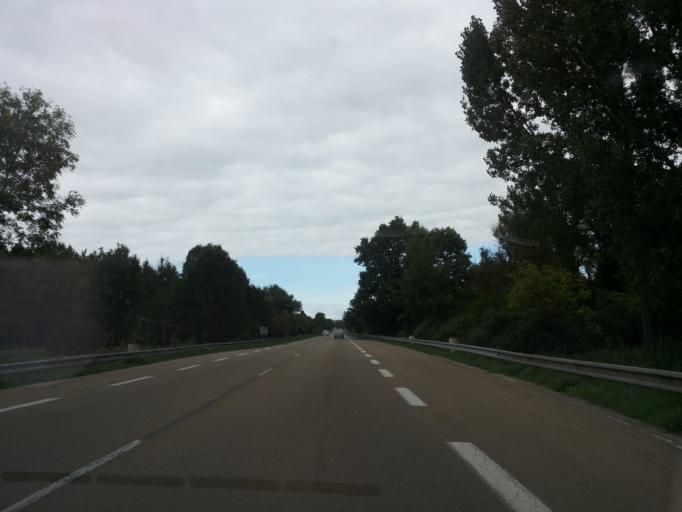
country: FR
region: Champagne-Ardenne
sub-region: Departement de la Marne
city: Sillery
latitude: 49.1941
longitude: 4.1548
